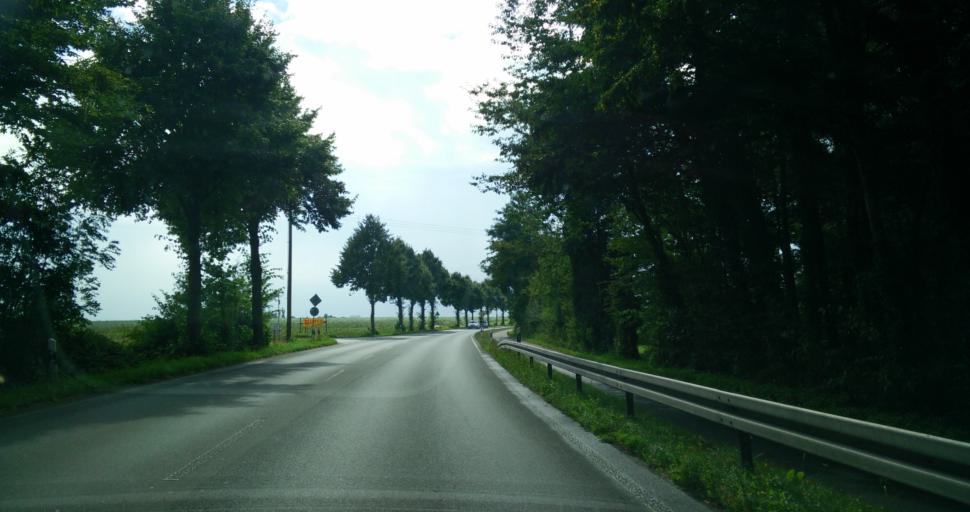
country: DE
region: North Rhine-Westphalia
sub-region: Regierungsbezirk Dusseldorf
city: Mettmann
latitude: 51.2309
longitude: 6.9935
